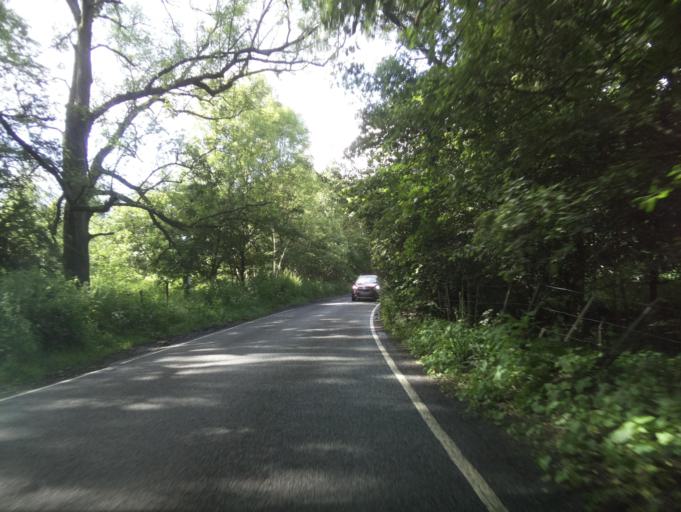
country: GB
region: England
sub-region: Hertfordshire
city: Kings Langley
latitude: 51.6743
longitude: -0.4433
